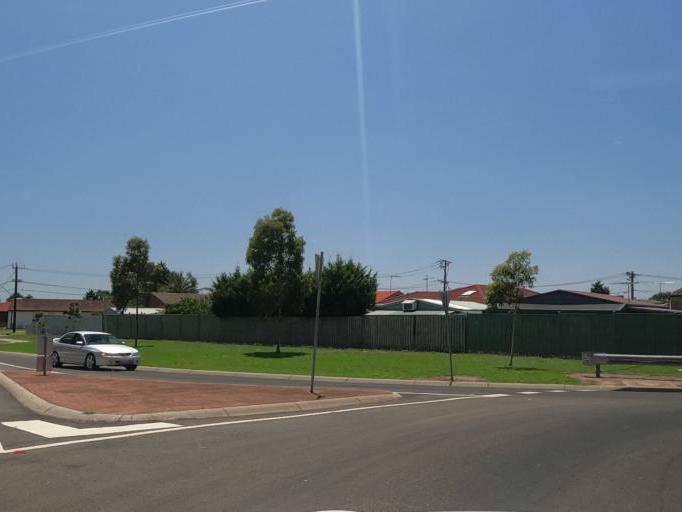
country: AU
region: Victoria
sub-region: Hume
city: Broadmeadows
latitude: -37.6747
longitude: 144.9199
